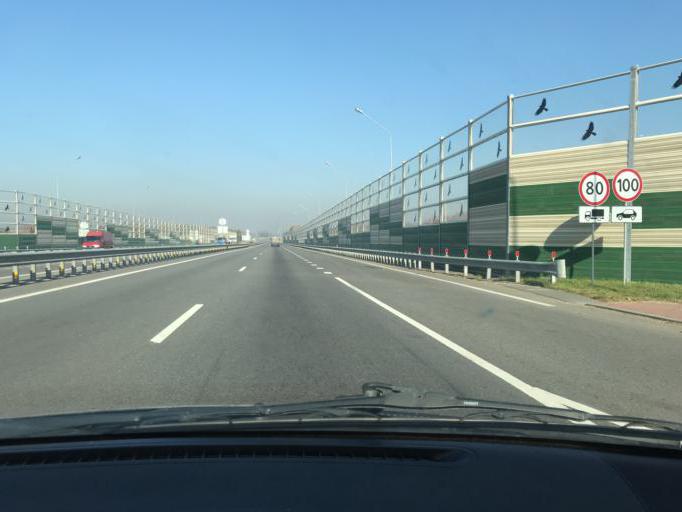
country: BY
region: Minsk
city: Slutsk
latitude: 53.2216
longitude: 27.5506
